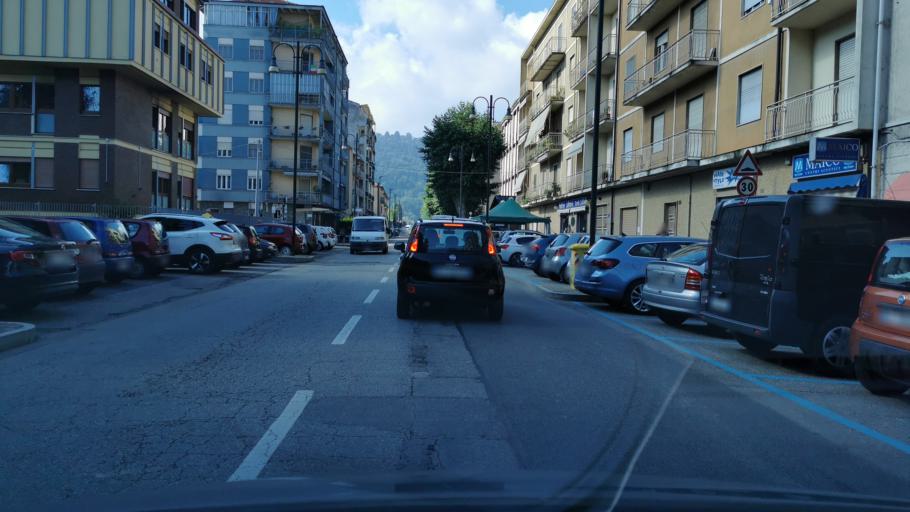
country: IT
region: Piedmont
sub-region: Provincia di Torino
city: Chivasso
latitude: 45.1874
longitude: 7.8896
